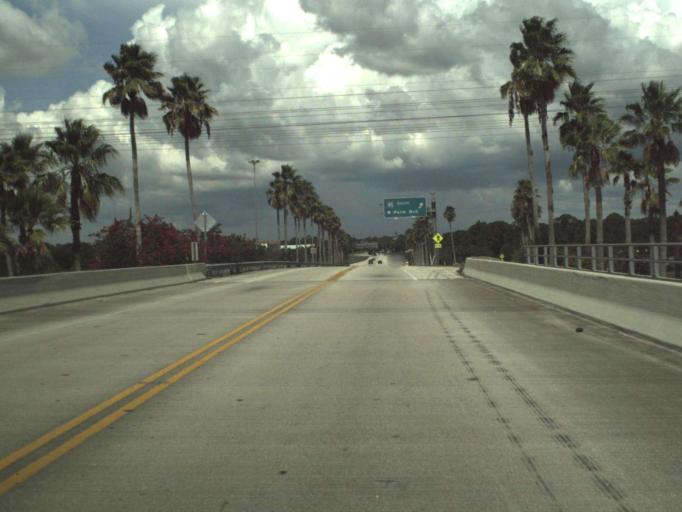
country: US
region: Florida
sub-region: Saint Lucie County
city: Port Saint Lucie
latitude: 27.3115
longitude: -80.4143
